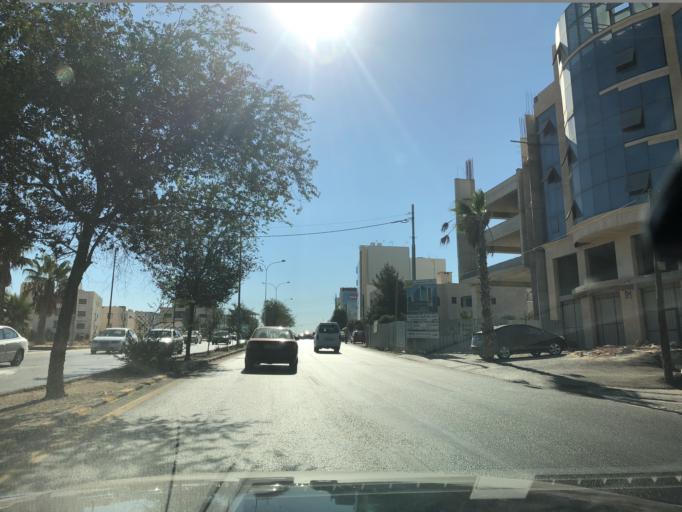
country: JO
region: Amman
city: Al Jubayhah
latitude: 31.9731
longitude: 35.8729
